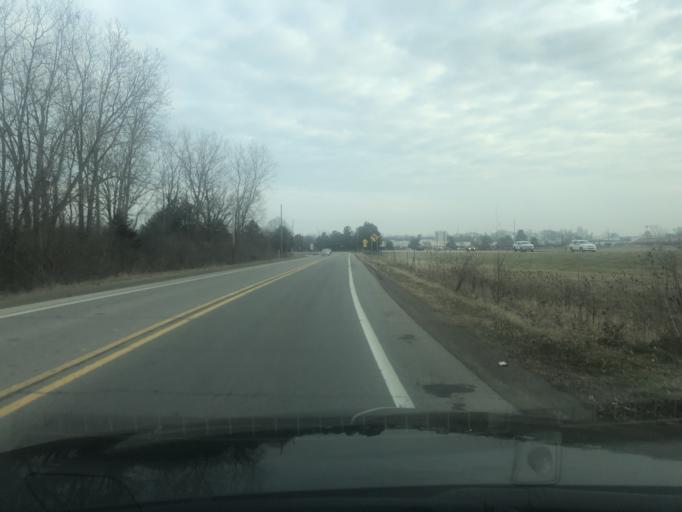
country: US
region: Michigan
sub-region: Wayne County
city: Belleville
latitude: 42.2208
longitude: -83.5452
